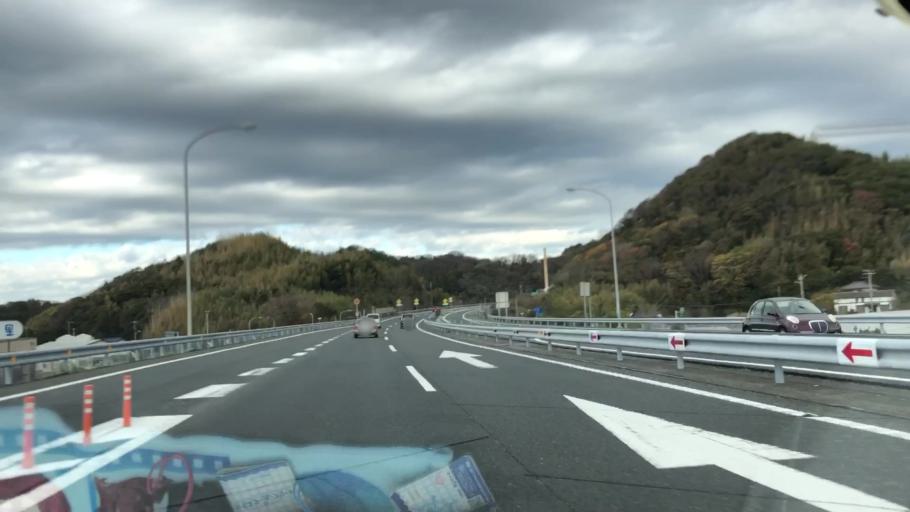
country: JP
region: Chiba
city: Tateyama
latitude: 35.1007
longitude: 139.8565
